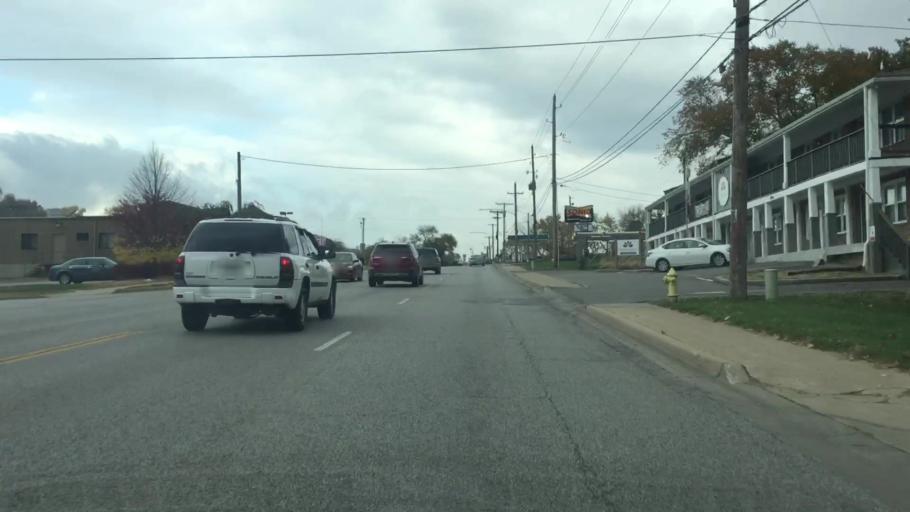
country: US
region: Missouri
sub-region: Jackson County
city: Raytown
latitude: 39.0032
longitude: -94.4636
